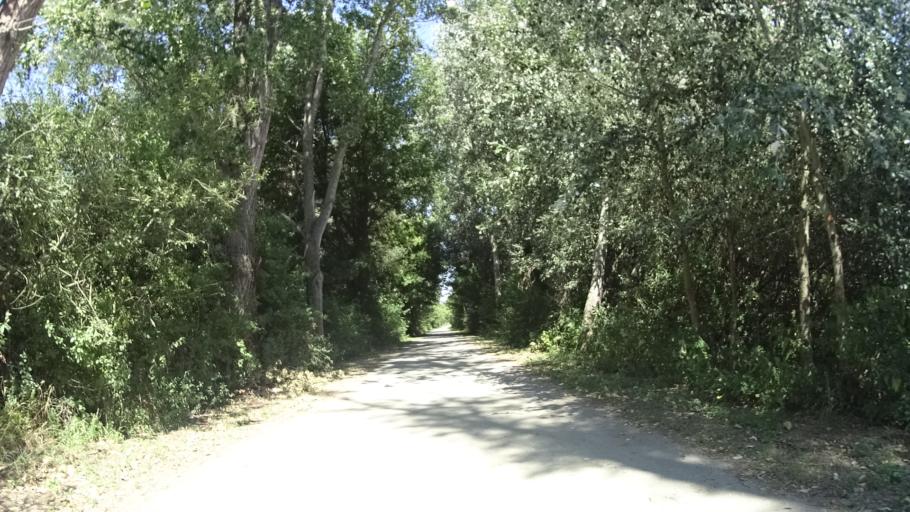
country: CZ
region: South Moravian
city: Straznice
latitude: 48.9149
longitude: 17.3283
